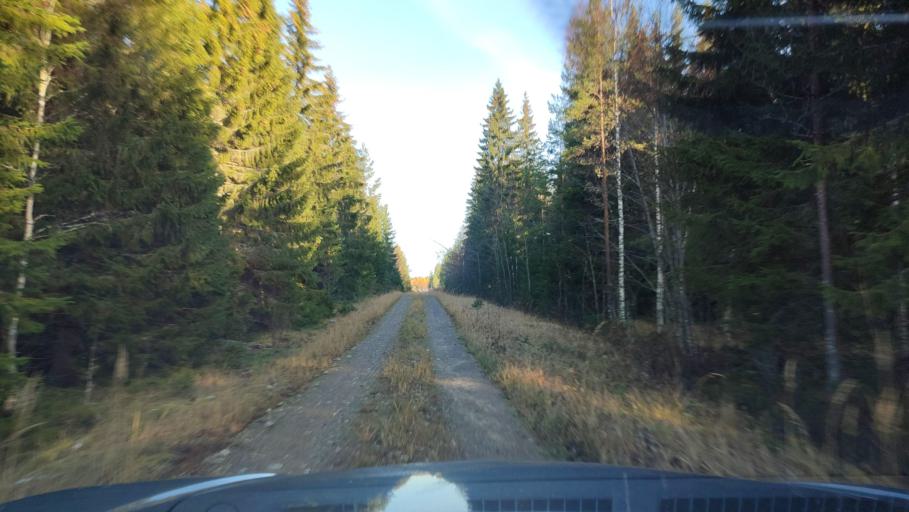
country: FI
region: Southern Ostrobothnia
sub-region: Suupohja
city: Karijoki
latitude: 62.1754
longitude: 21.6065
